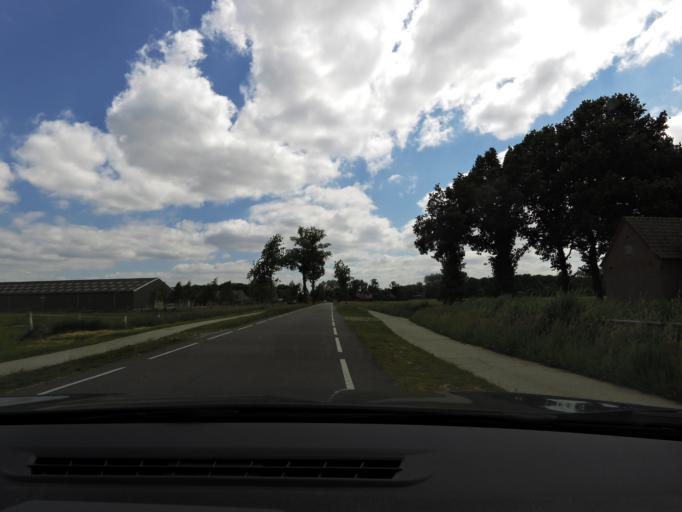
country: NL
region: North Brabant
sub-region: Gemeente Loon op Zand
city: Loon op Zand
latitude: 51.6291
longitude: 5.1163
